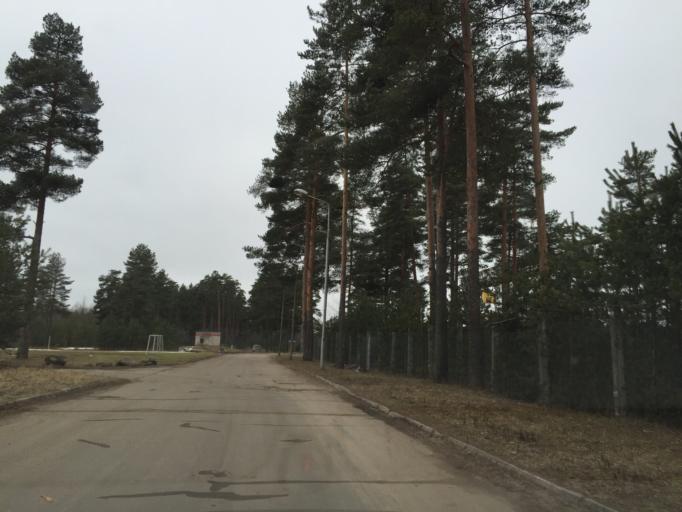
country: LV
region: Garkalne
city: Garkalne
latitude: 56.9612
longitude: 24.4255
